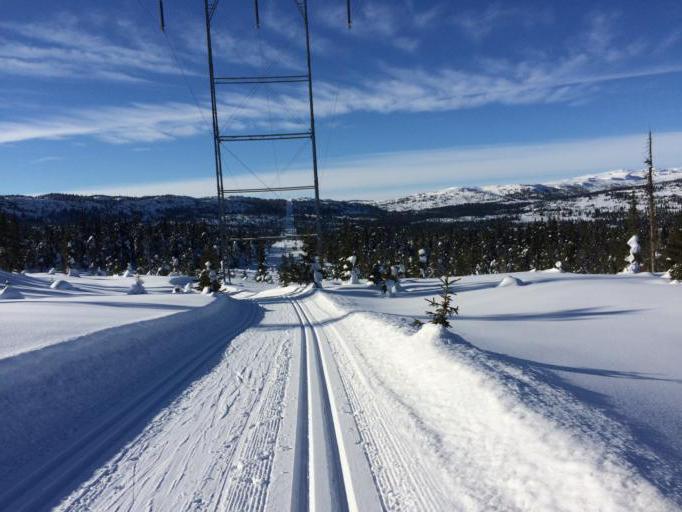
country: NO
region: Oppland
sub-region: Gausdal
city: Segalstad bru
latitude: 61.3183
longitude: 10.0934
